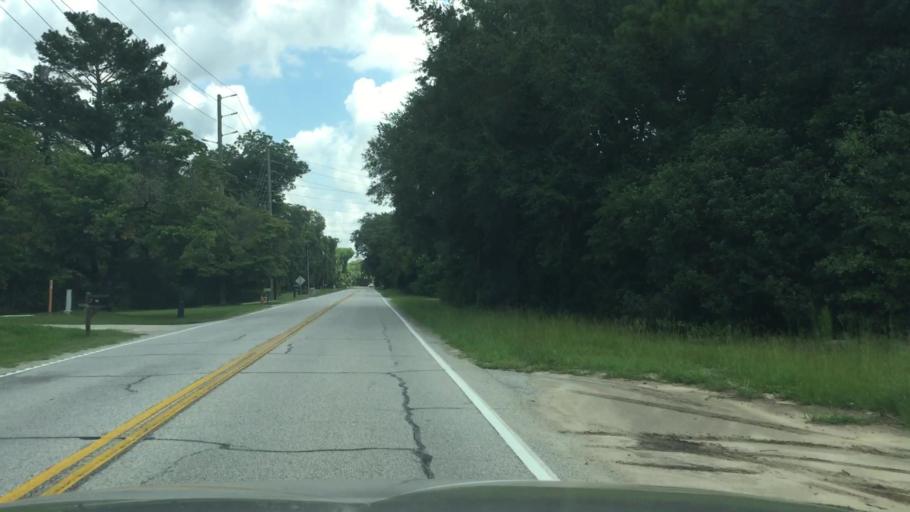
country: US
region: South Carolina
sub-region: Sumter County
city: South Sumter
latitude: 33.9134
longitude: -80.3941
